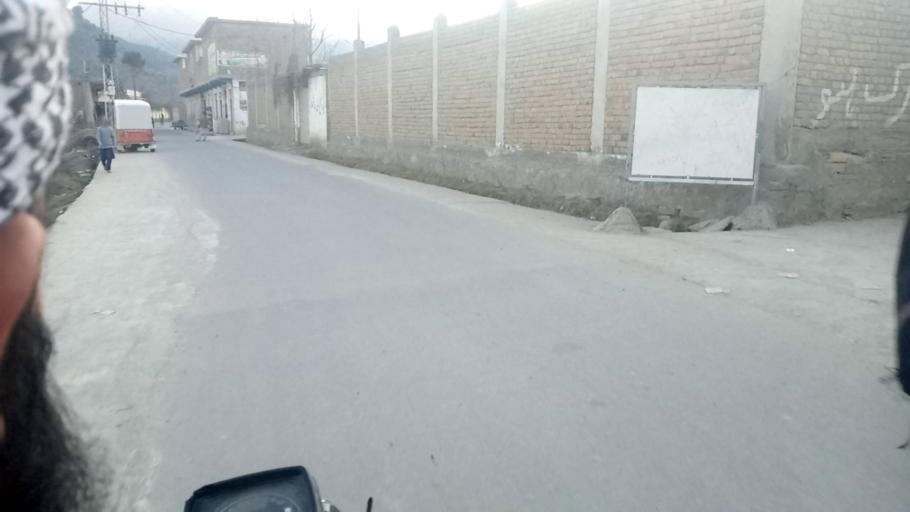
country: PK
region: Khyber Pakhtunkhwa
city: Saidu Sharif
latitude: 34.7406
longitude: 72.3375
